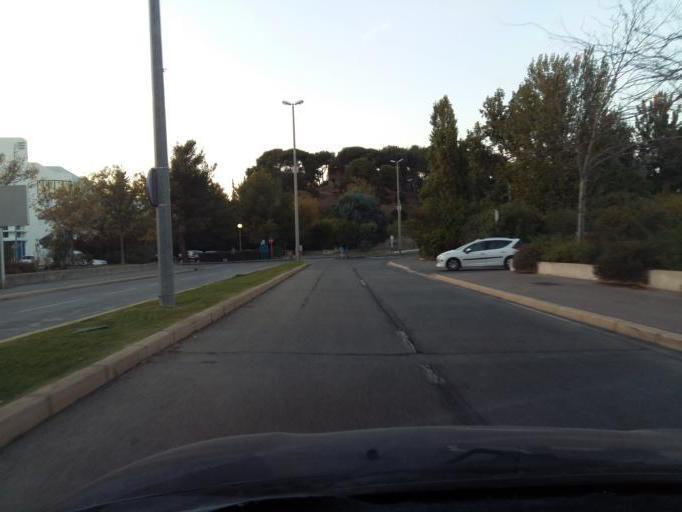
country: FR
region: Provence-Alpes-Cote d'Azur
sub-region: Departement des Bouches-du-Rhone
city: Martigues
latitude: 43.4065
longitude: 5.0471
